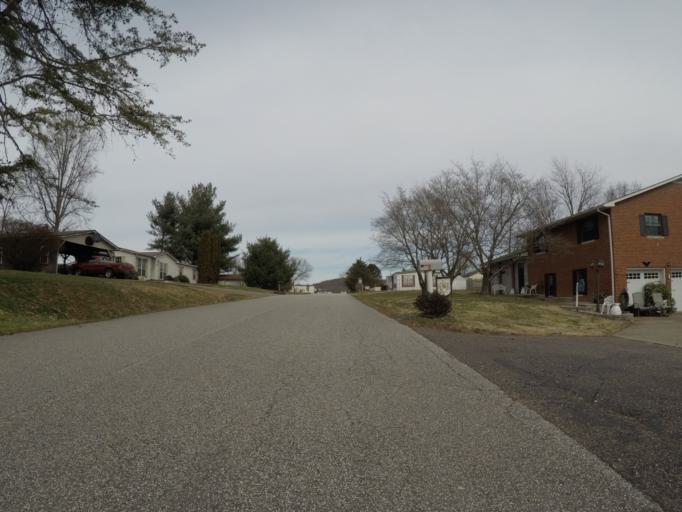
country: US
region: West Virginia
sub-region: Cabell County
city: Pea Ridge
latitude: 38.4490
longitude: -82.3473
